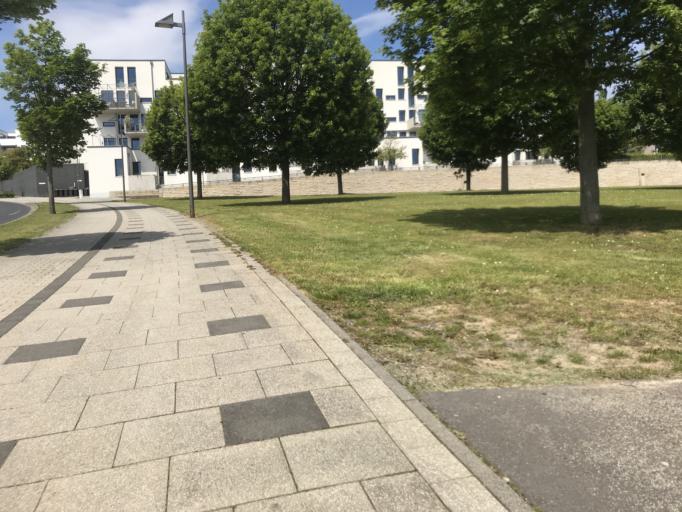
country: DE
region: Hesse
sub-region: Regierungsbezirk Darmstadt
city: Bad Homburg vor der Hoehe
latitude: 50.1775
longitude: 8.6403
